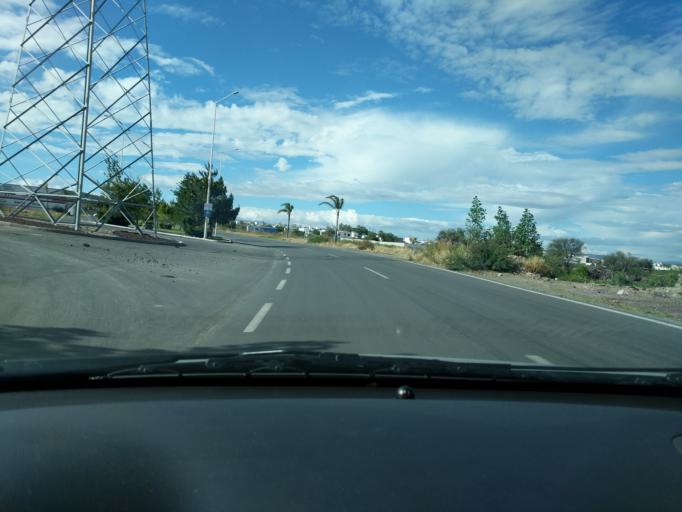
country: MX
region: Queretaro
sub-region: El Marques
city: Paseos del Marques
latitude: 20.5948
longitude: -100.2763
